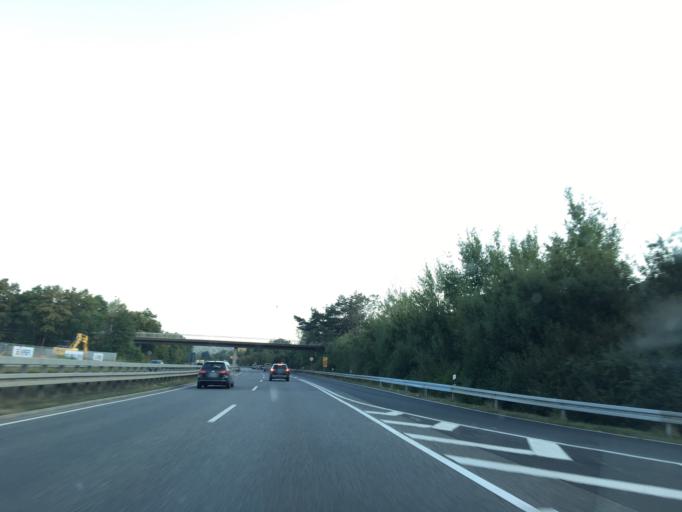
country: DE
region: Hesse
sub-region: Regierungsbezirk Giessen
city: Marburg an der Lahn
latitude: 50.8264
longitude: 8.7673
